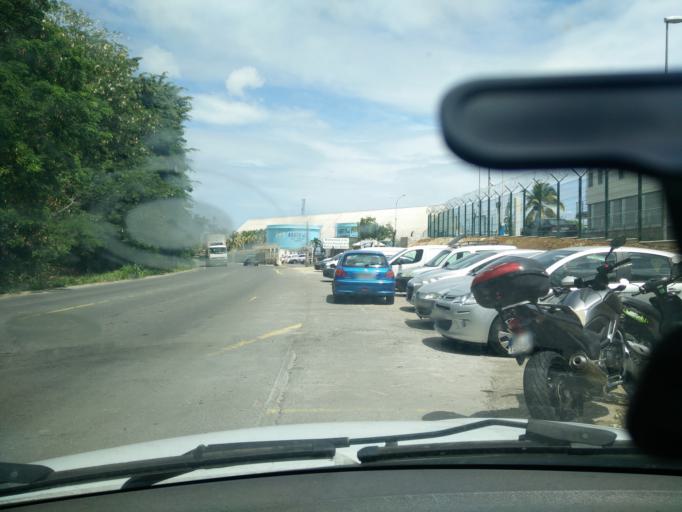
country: GP
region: Guadeloupe
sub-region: Guadeloupe
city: Pointe-a-Pitre
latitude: 16.2332
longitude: -61.5533
